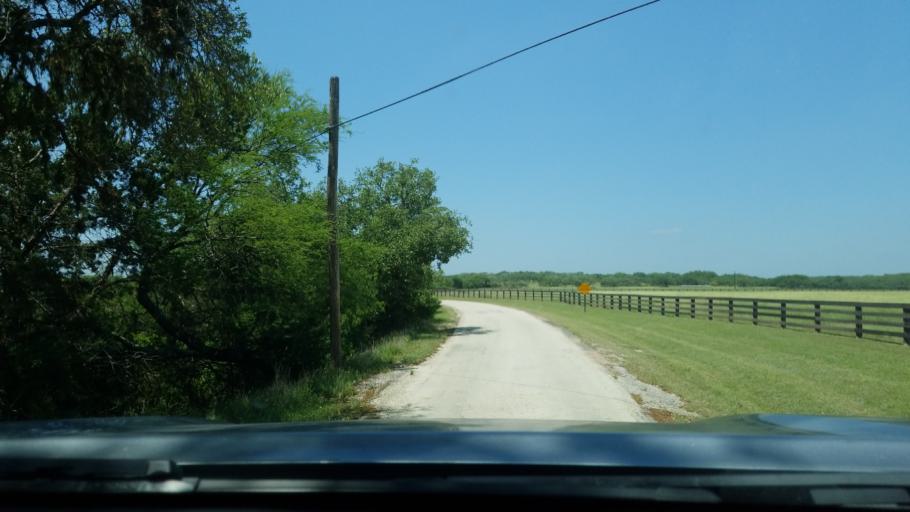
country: US
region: Texas
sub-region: Blanco County
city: Blanco
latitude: 30.0070
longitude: -98.4362
